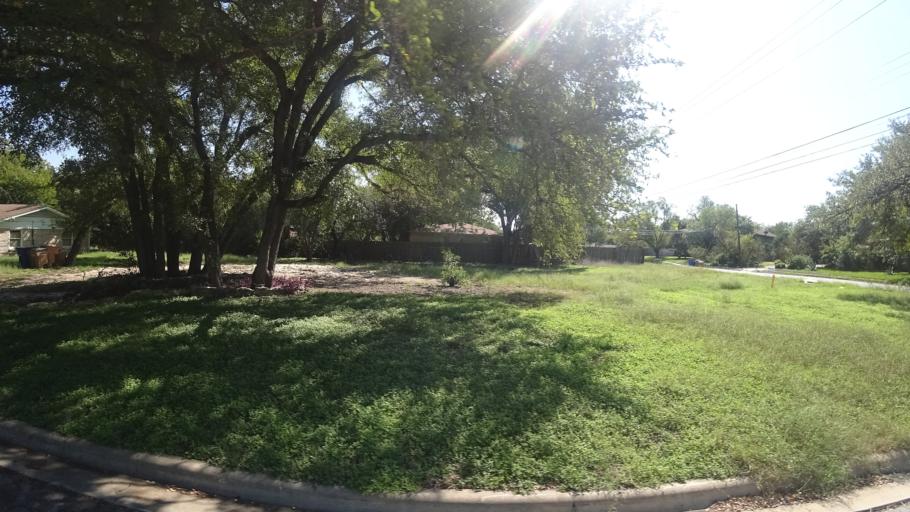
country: US
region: Texas
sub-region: Travis County
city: Austin
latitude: 30.3105
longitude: -97.6734
